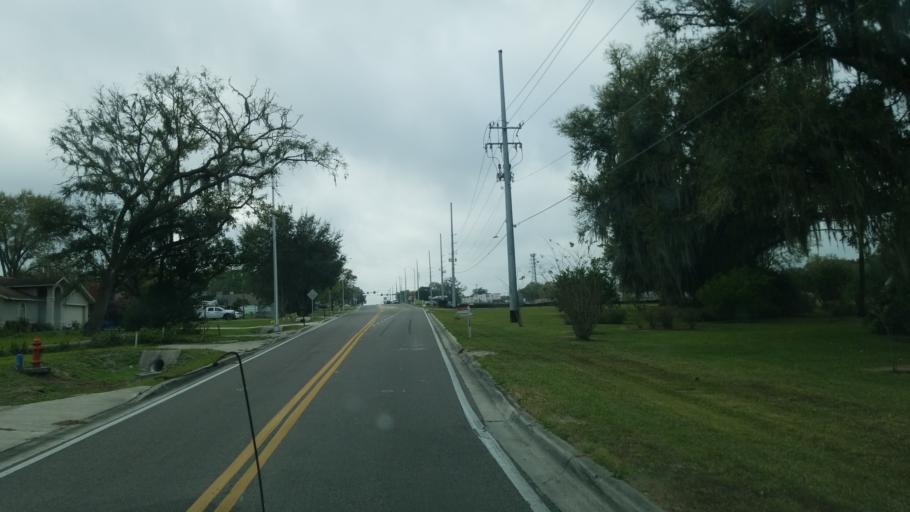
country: US
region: Florida
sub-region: Polk County
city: Kathleen
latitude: 28.1389
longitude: -82.0233
